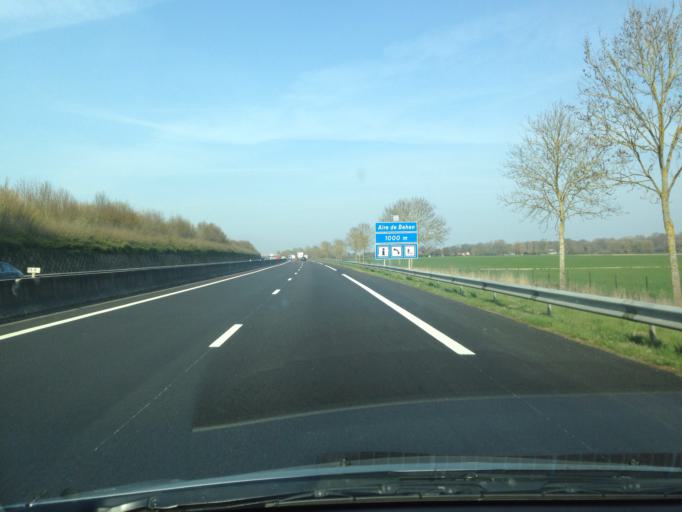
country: FR
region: Picardie
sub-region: Departement de la Somme
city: Oisemont
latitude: 50.0345
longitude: 1.7492
